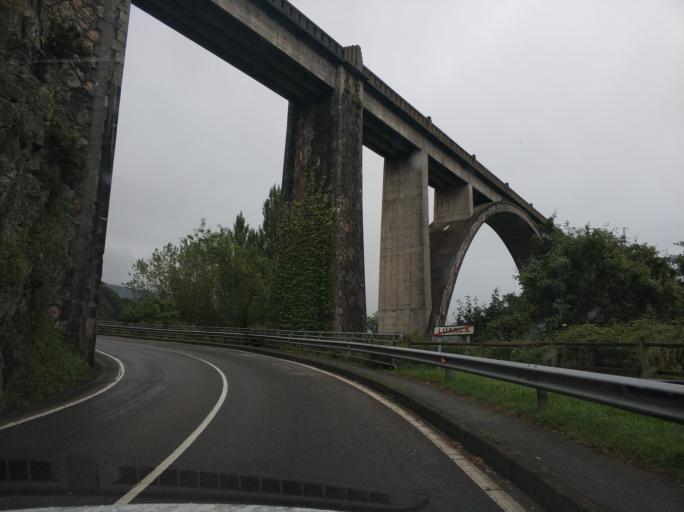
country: ES
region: Asturias
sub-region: Province of Asturias
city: Navia
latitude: 43.5400
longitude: -6.5351
